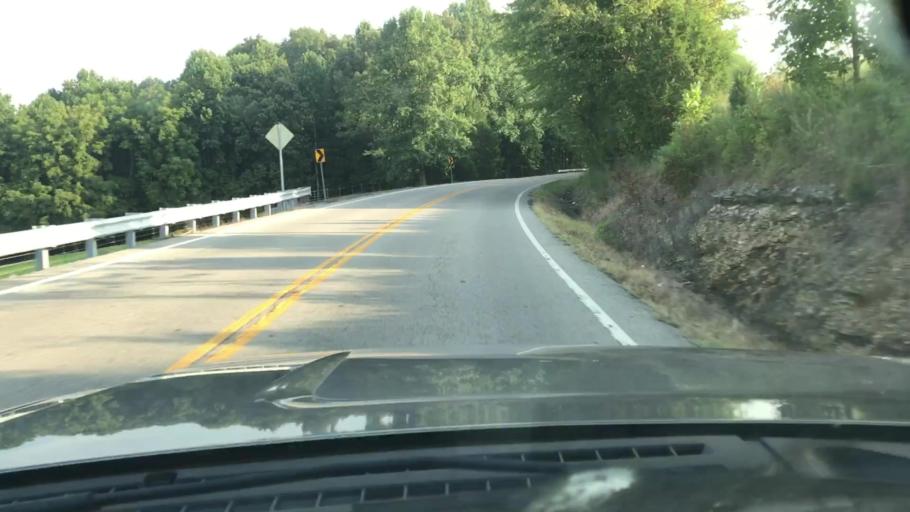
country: US
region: Tennessee
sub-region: Sumner County
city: Portland
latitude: 36.5191
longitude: -86.4236
